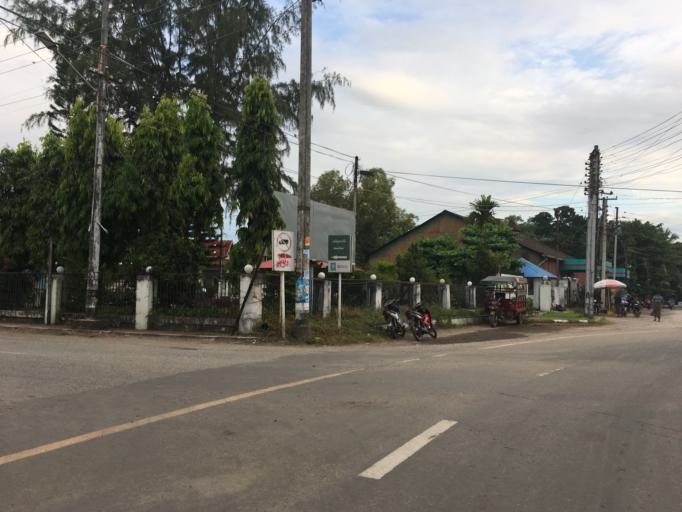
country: MM
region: Mon
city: Mawlamyine
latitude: 16.4984
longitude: 97.6194
